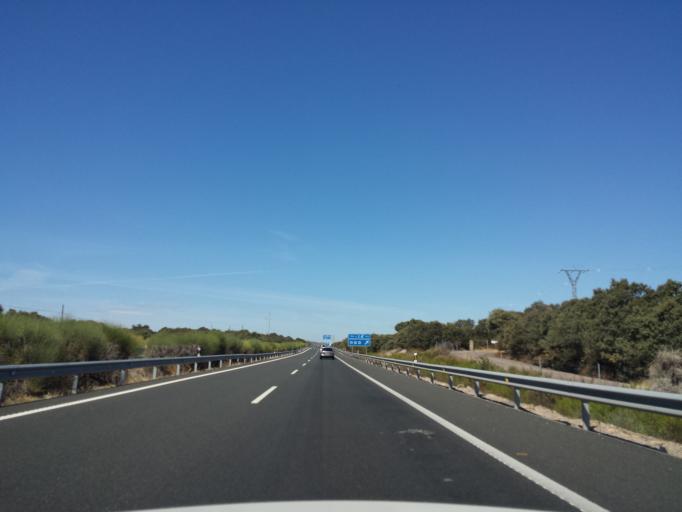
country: ES
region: Extremadura
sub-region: Provincia de Caceres
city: Peraleda de la Mata
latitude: 39.8899
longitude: -5.4505
